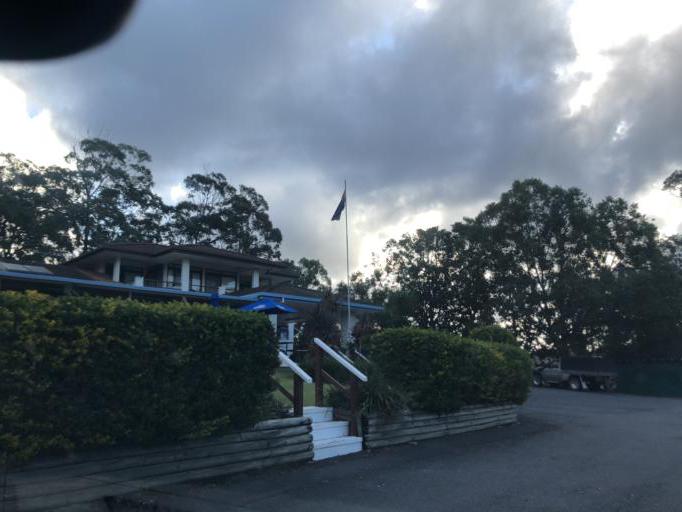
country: AU
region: New South Wales
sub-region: Coffs Harbour
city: Woolgoolga
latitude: -30.0943
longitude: 153.1940
